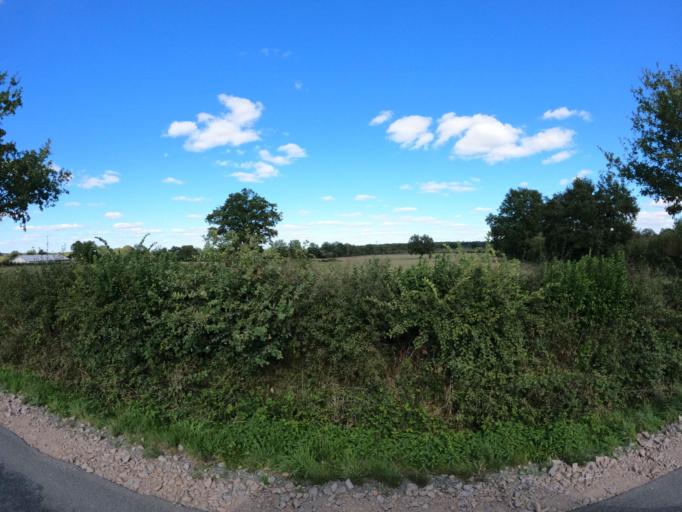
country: FR
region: Auvergne
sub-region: Departement de l'Allier
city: Doyet
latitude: 46.3887
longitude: 2.7644
